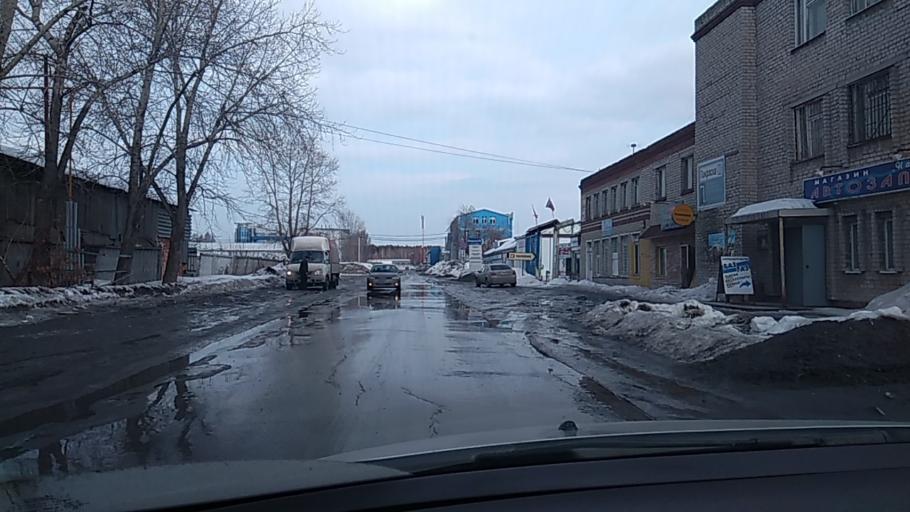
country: RU
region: Sverdlovsk
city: Yekaterinburg
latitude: 56.8617
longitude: 60.6663
